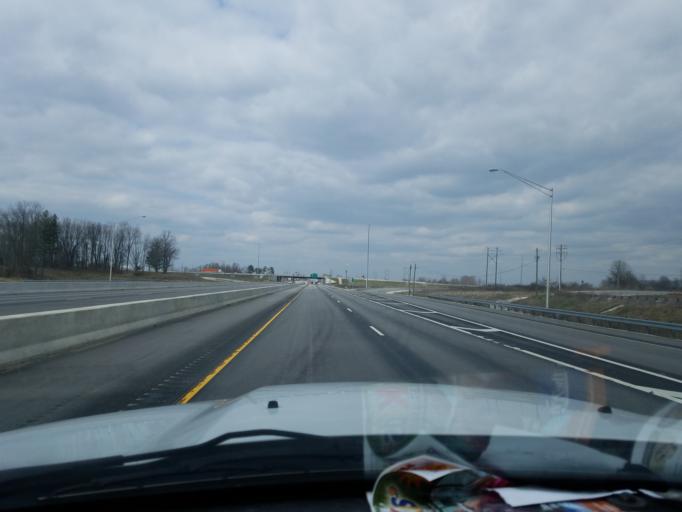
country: US
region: Indiana
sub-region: Vigo County
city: Terre Haute
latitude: 39.4258
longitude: -87.3329
